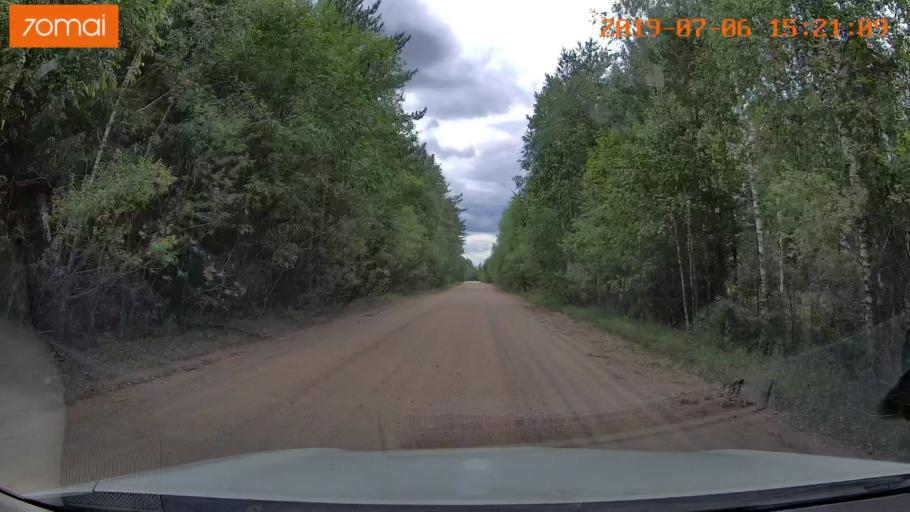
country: BY
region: Minsk
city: Valozhyn
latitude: 54.0096
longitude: 26.6204
